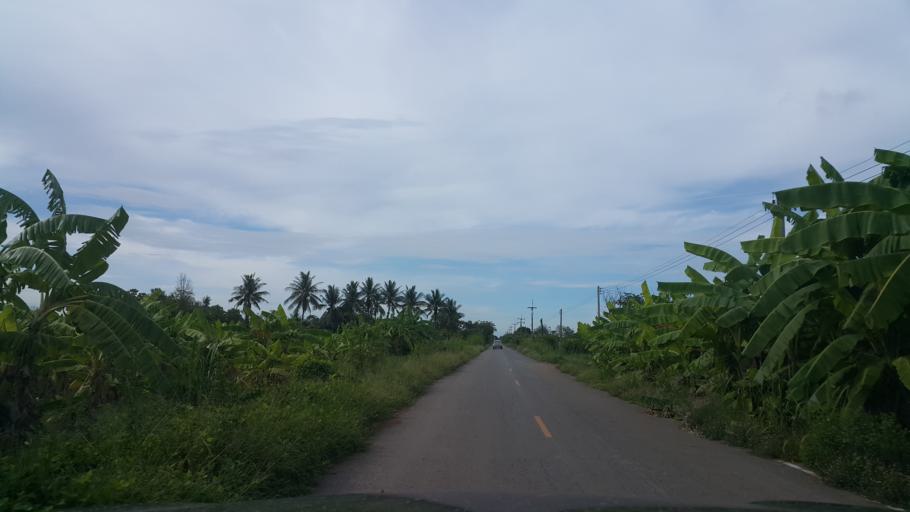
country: TH
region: Sukhothai
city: Sawankhalok
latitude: 17.2722
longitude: 99.9066
